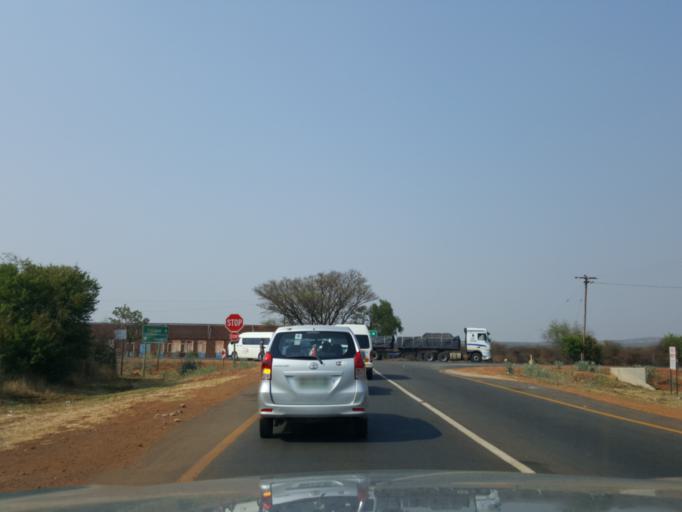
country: ZA
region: North-West
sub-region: Ngaka Modiri Molema District Municipality
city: Zeerust
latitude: -25.5038
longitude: 25.9836
